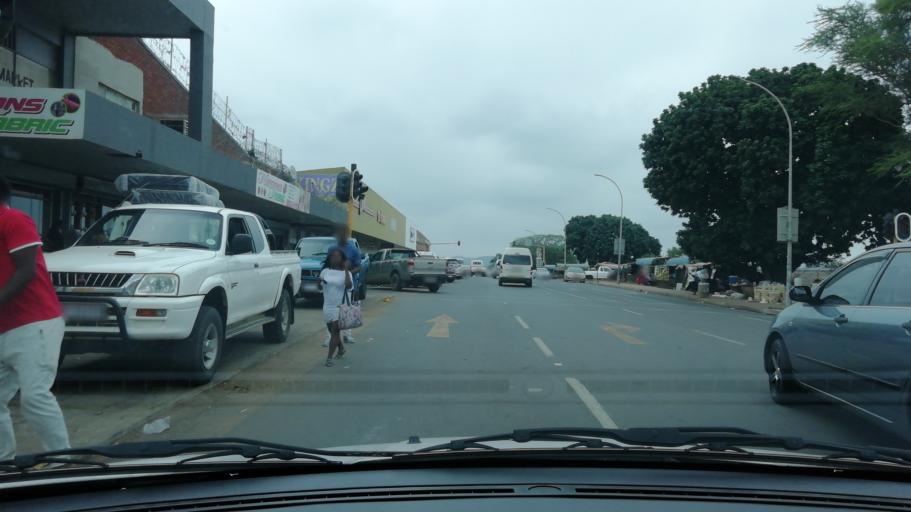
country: ZA
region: KwaZulu-Natal
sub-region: uThungulu District Municipality
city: Empangeni
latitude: -28.7433
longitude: 31.8898
